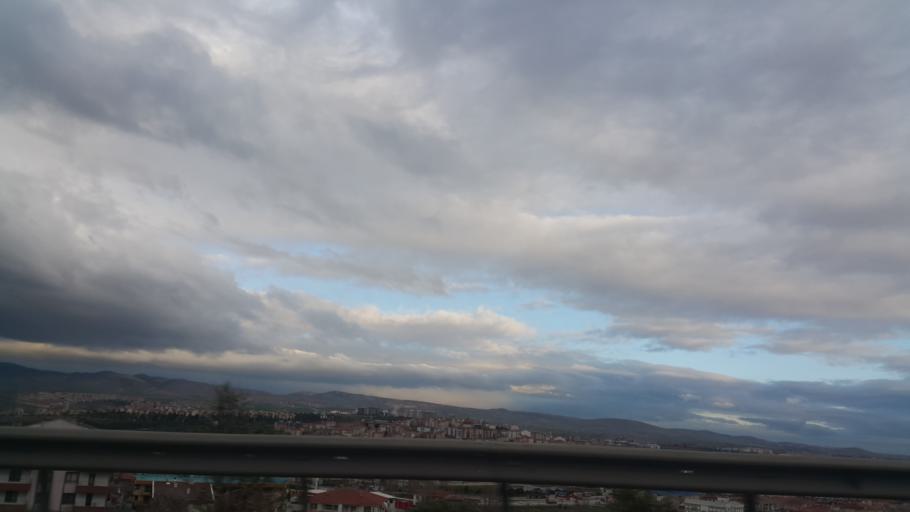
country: TR
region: Ankara
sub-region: Goelbasi
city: Golbasi
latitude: 39.8068
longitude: 32.8002
